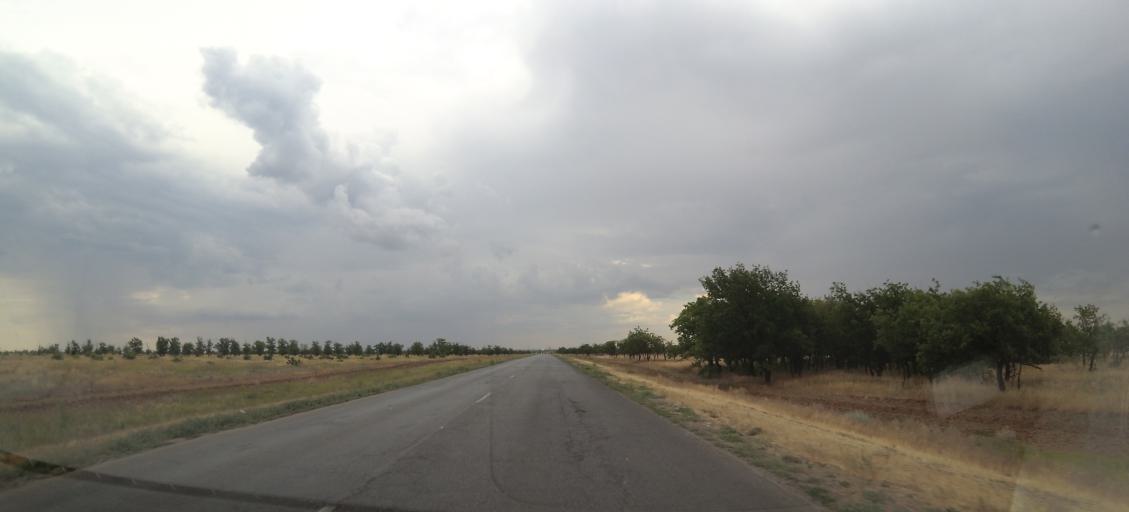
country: RU
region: Volgograd
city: Kotel'nikovo
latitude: 47.6118
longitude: 43.1139
